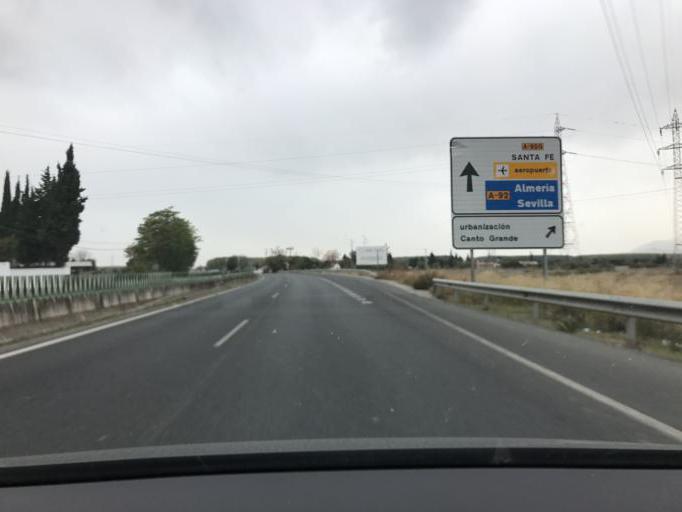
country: ES
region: Andalusia
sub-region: Provincia de Granada
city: Maracena
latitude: 37.1920
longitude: -3.6669
